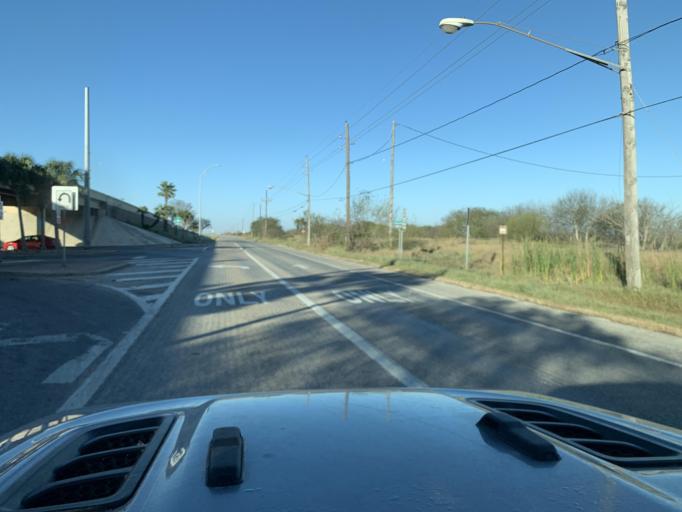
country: US
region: Texas
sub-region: Nueces County
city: Corpus Christi
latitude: 27.7852
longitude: -97.5019
